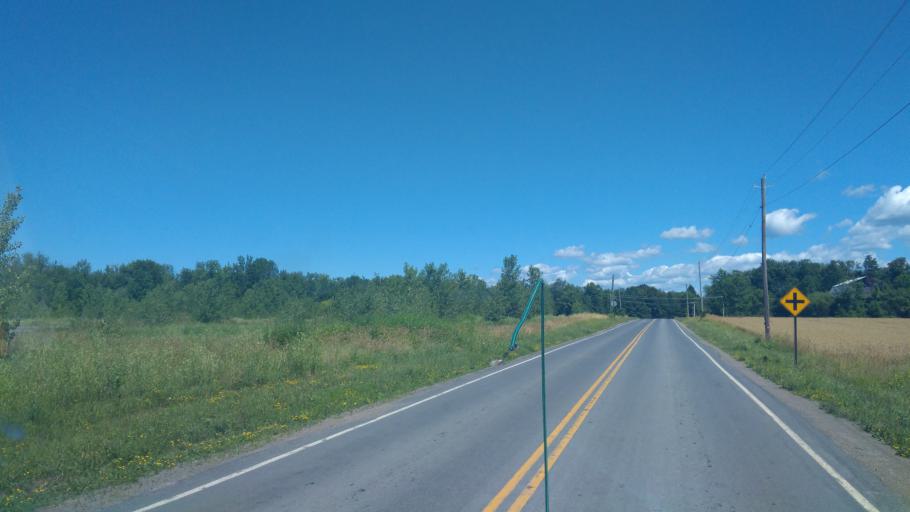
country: US
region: New York
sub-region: Wayne County
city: Sodus
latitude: 43.1830
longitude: -77.0352
